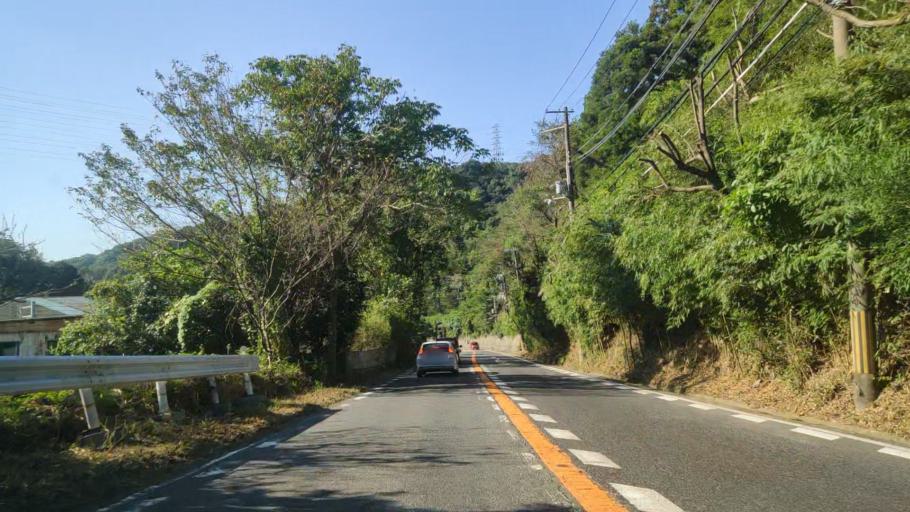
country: JP
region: Hyogo
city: Kobe
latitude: 34.7089
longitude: 135.1611
